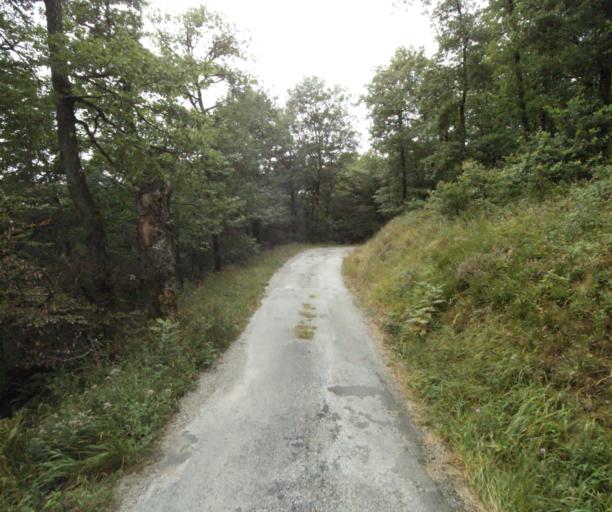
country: FR
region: Midi-Pyrenees
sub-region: Departement du Tarn
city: Soreze
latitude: 43.4334
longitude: 2.0896
